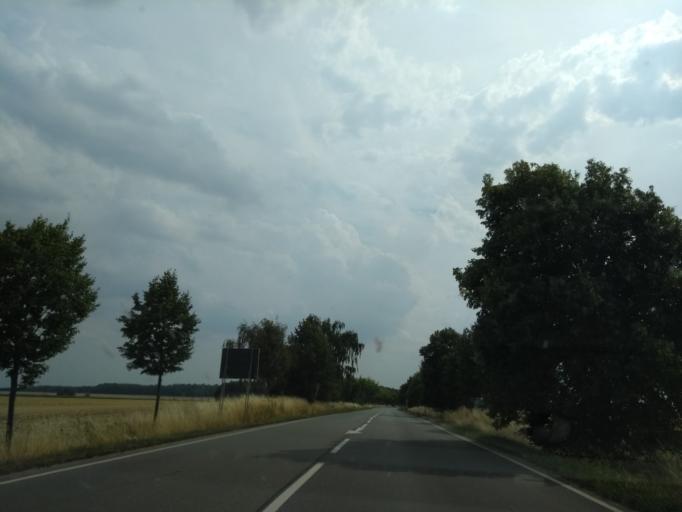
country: DE
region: Thuringia
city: Hirschfeld
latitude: 50.9804
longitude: 12.1357
